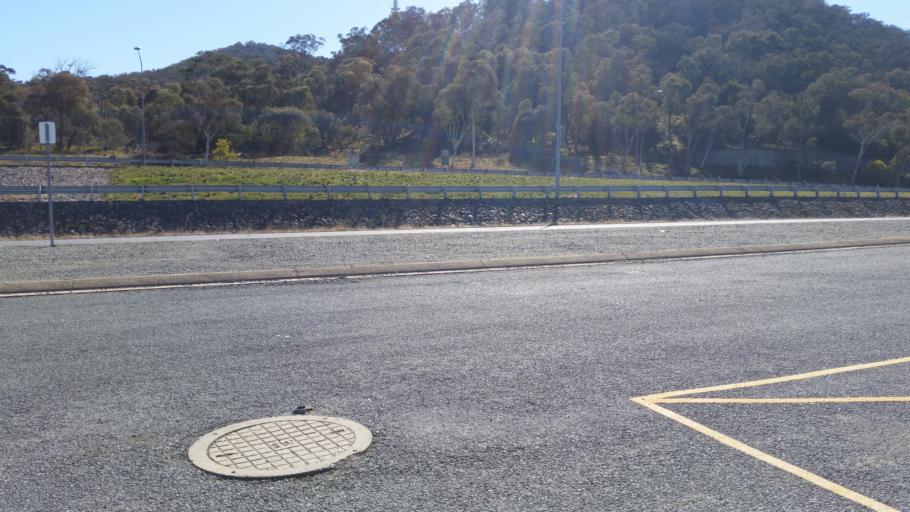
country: AU
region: Australian Capital Territory
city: Acton
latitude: -35.2857
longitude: 149.0907
